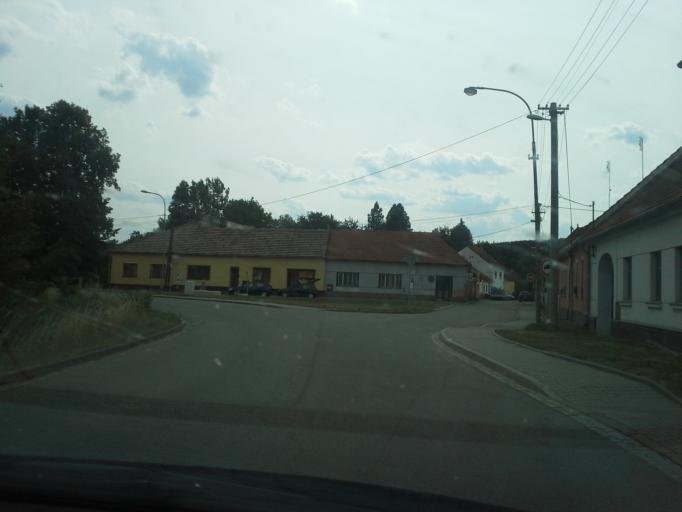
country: CZ
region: South Moravian
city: Svitavka
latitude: 49.5065
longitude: 16.5946
